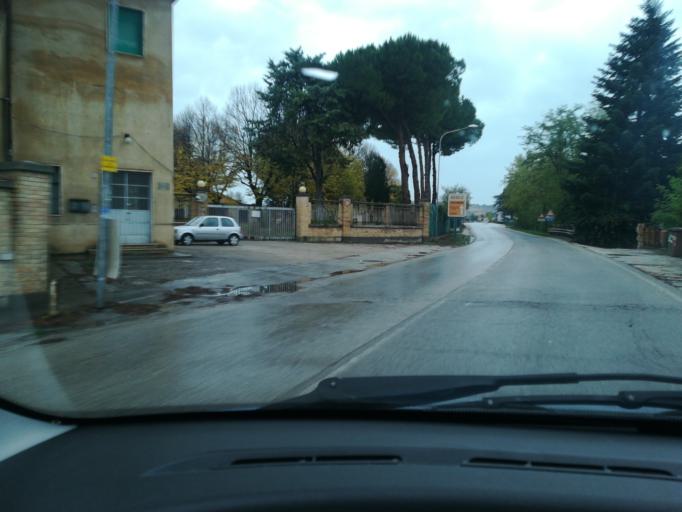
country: IT
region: The Marches
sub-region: Provincia di Macerata
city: Borgo Stazione
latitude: 43.2874
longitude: 13.6498
